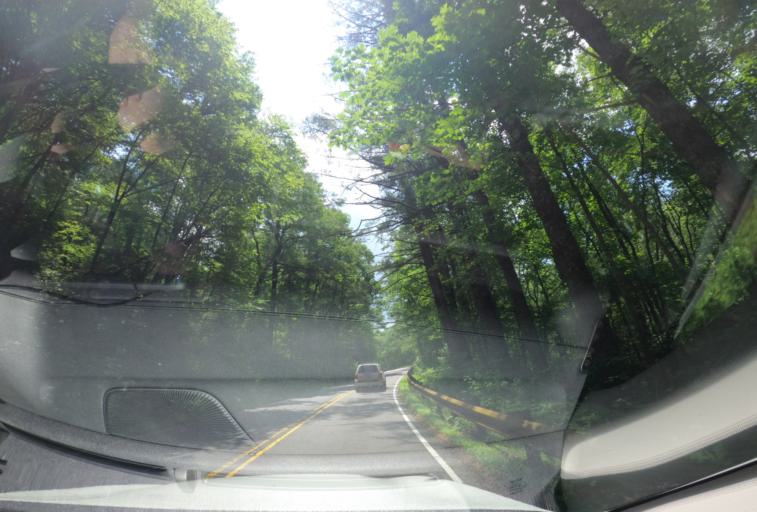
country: US
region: North Carolina
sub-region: Macon County
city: Franklin
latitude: 35.0692
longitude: -83.2286
